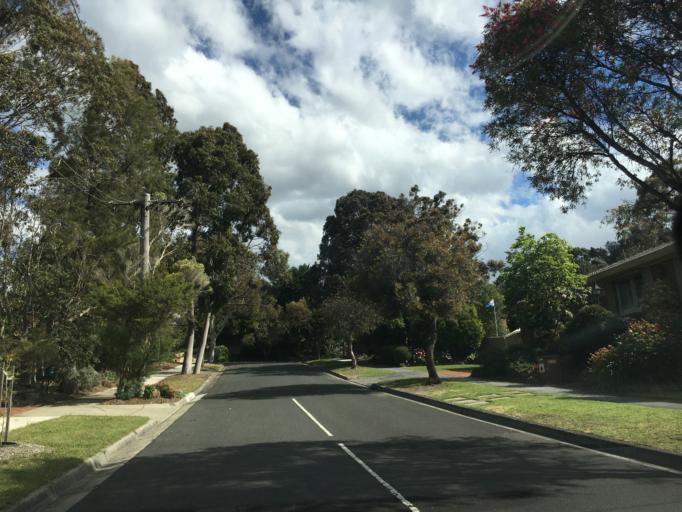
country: AU
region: Victoria
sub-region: Whitehorse
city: Vermont South
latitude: -37.8870
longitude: 145.1781
